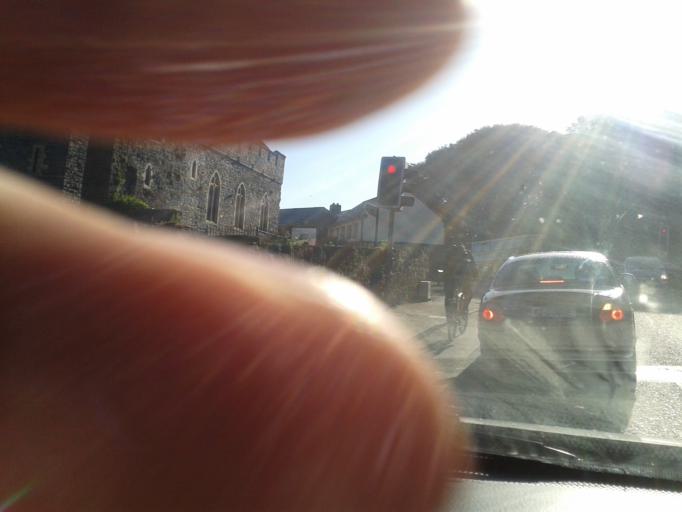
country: IE
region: Leinster
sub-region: Fingal County
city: Swords
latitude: 53.4595
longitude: -6.2208
